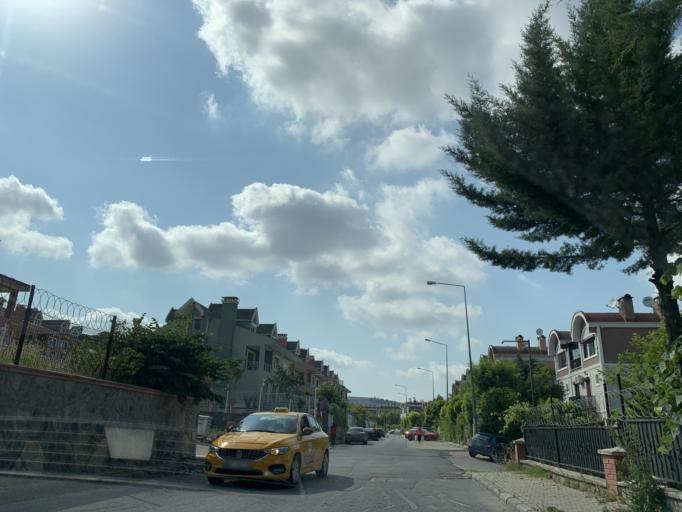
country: TR
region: Istanbul
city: Esenyurt
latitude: 41.0833
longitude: 28.6747
